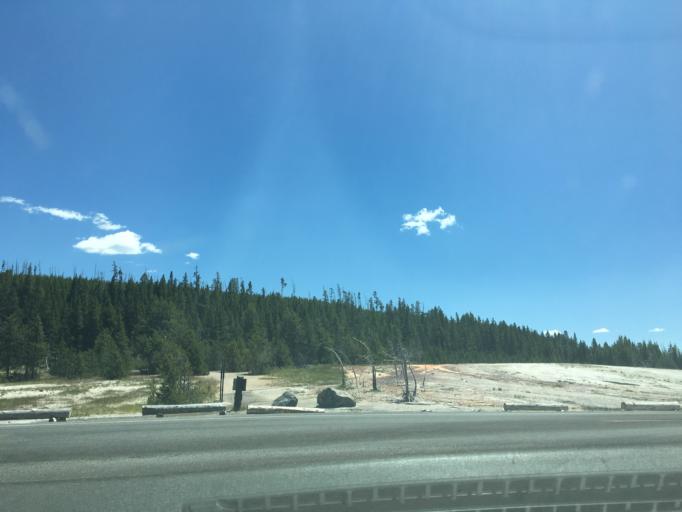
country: US
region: Montana
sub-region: Gallatin County
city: West Yellowstone
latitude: 44.4842
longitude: -110.8516
